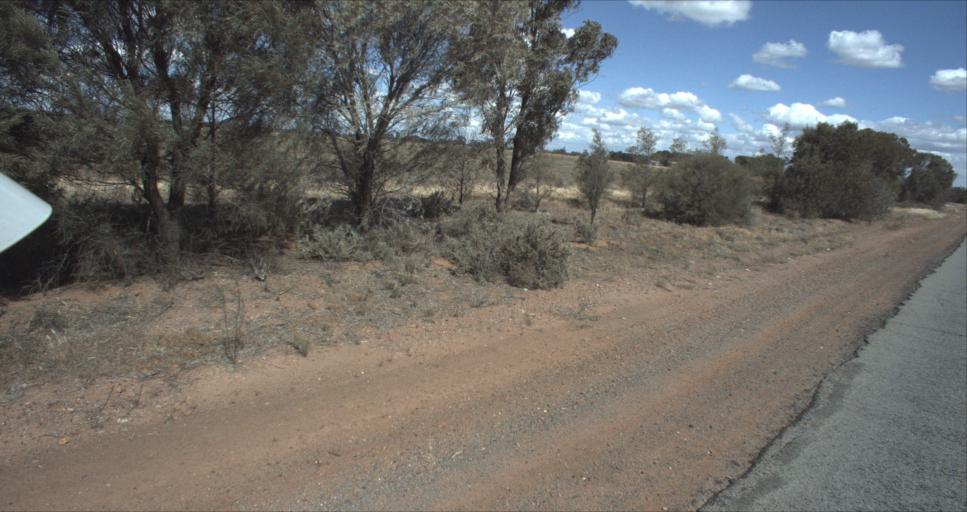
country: AU
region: New South Wales
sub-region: Leeton
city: Leeton
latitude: -34.4760
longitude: 146.2500
